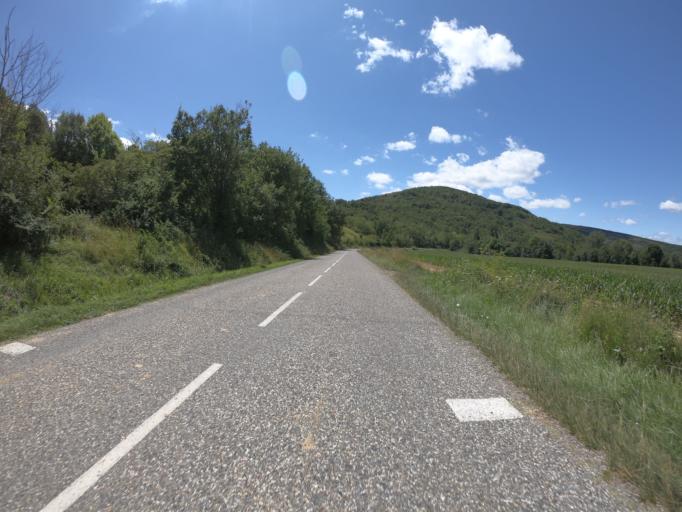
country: FR
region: Midi-Pyrenees
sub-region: Departement de l'Ariege
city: Mirepoix
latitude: 43.0447
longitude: 1.7780
